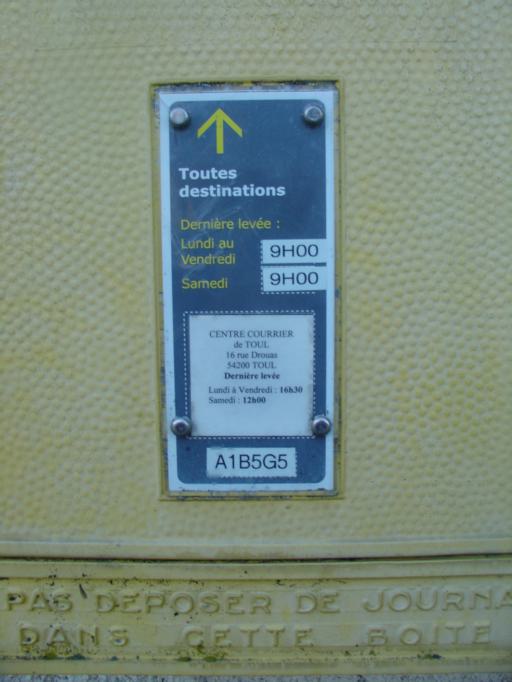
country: FR
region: Lorraine
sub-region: Departement de Meurthe-et-Moselle
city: Foug
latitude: 48.7497
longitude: 5.7630
